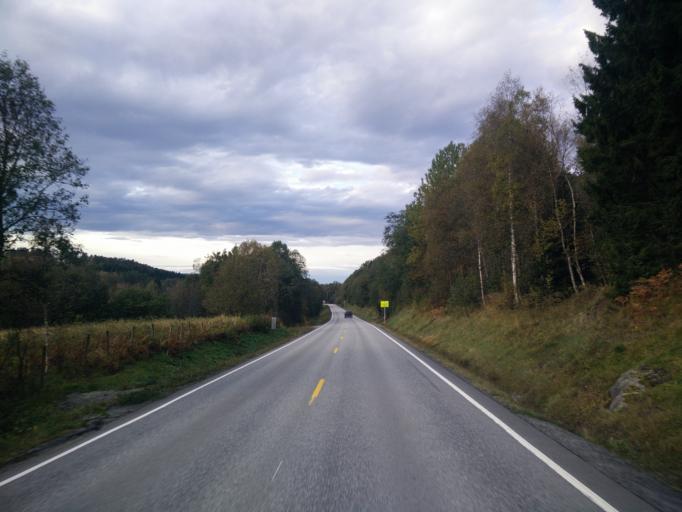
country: NO
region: More og Romsdal
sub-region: Molde
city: Hjelset
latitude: 62.7930
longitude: 7.5363
